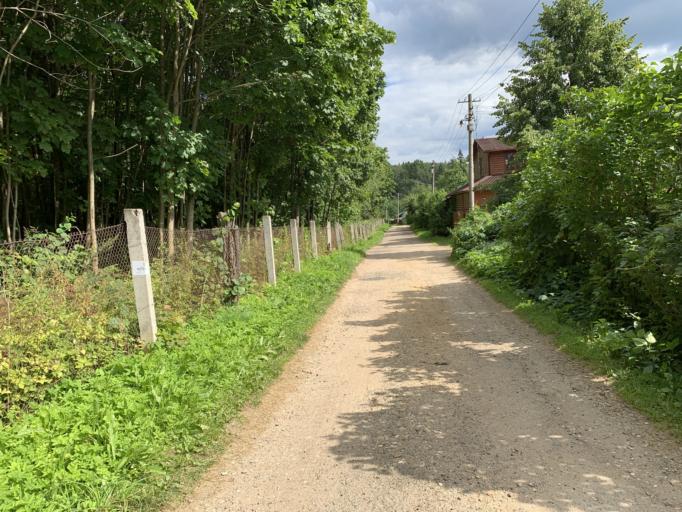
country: RU
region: Moskovskaya
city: Podosinki
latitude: 56.1799
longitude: 37.5784
